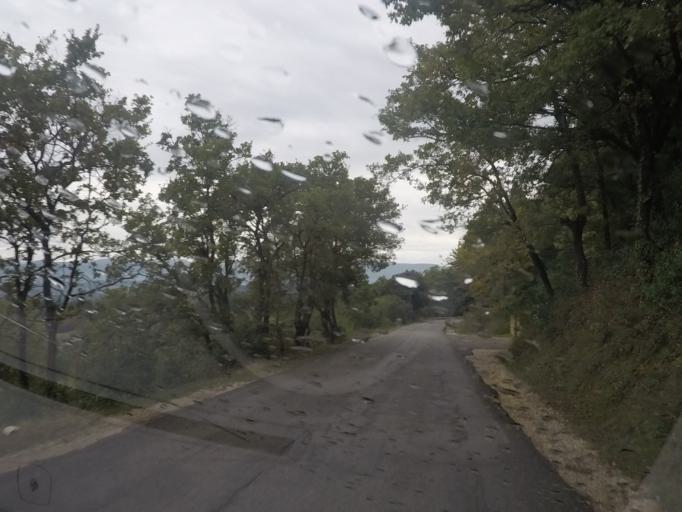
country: FR
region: Provence-Alpes-Cote d'Azur
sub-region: Departement du Vaucluse
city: Bonnieux
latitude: 43.8254
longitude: 5.3118
